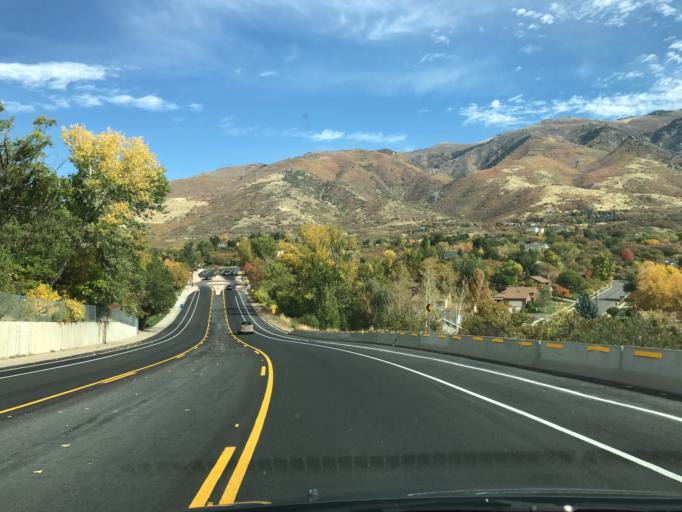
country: US
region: Utah
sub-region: Davis County
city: South Weber
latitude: 41.0893
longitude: -111.9205
